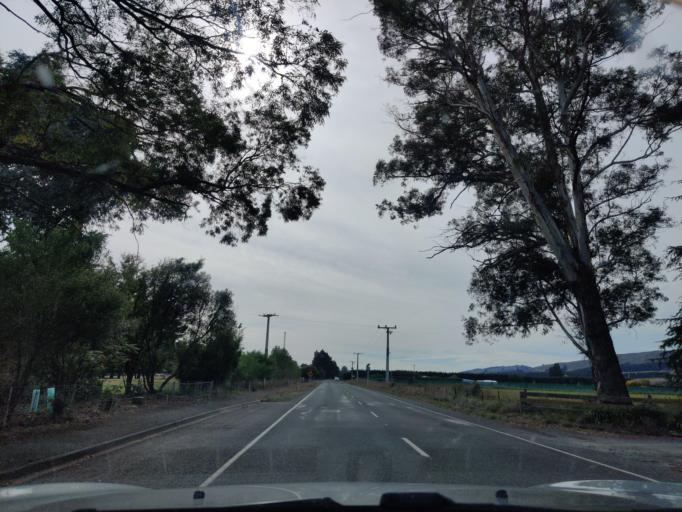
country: NZ
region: Nelson
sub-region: Nelson City
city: Nelson
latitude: -41.5621
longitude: 173.5380
